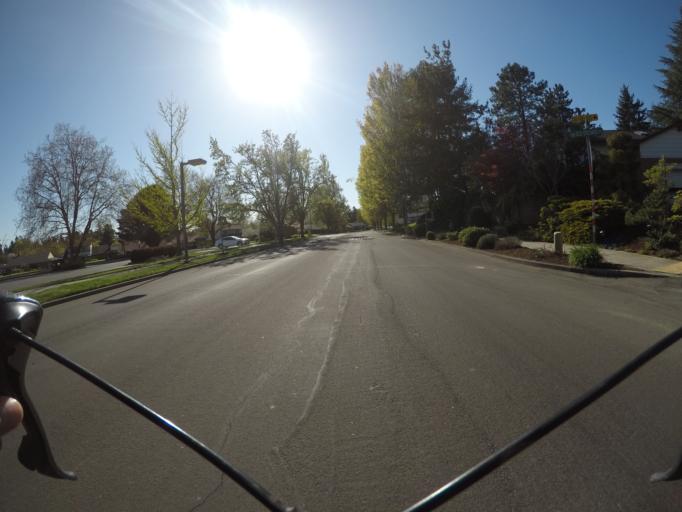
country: US
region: Oregon
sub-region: Washington County
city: King City
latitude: 45.4062
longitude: -122.7874
